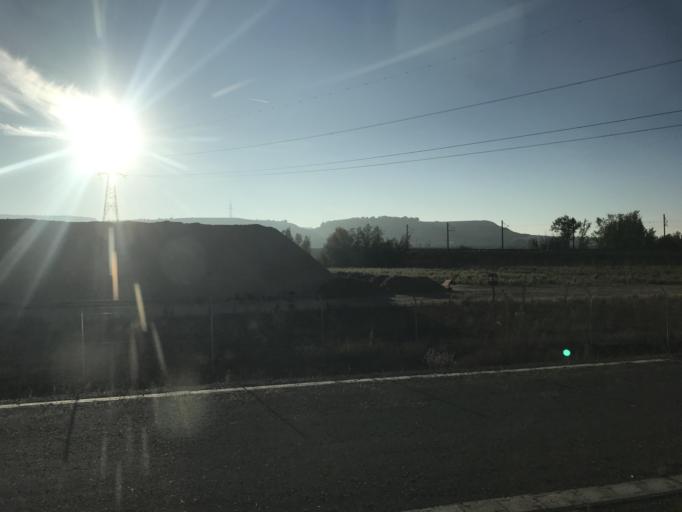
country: ES
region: Castille and Leon
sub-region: Provincia de Valladolid
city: Santovenia de Pisuerga
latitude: 41.6998
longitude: -4.6766
